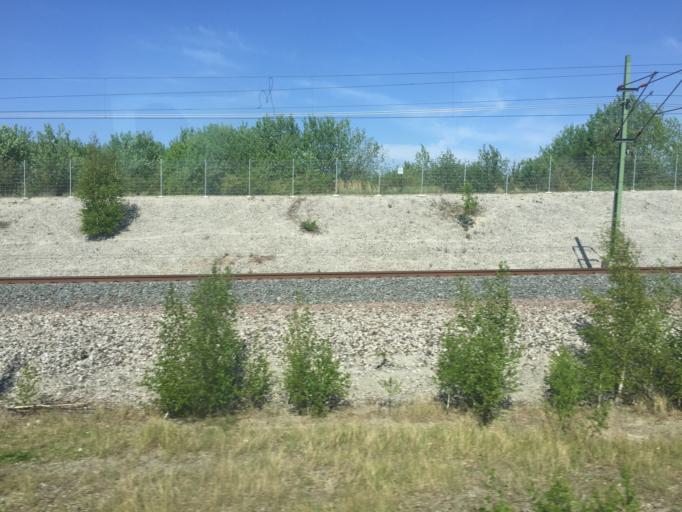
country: SE
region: Skane
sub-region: Malmo
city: Bunkeflostrand
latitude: 55.5585
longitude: 12.9512
